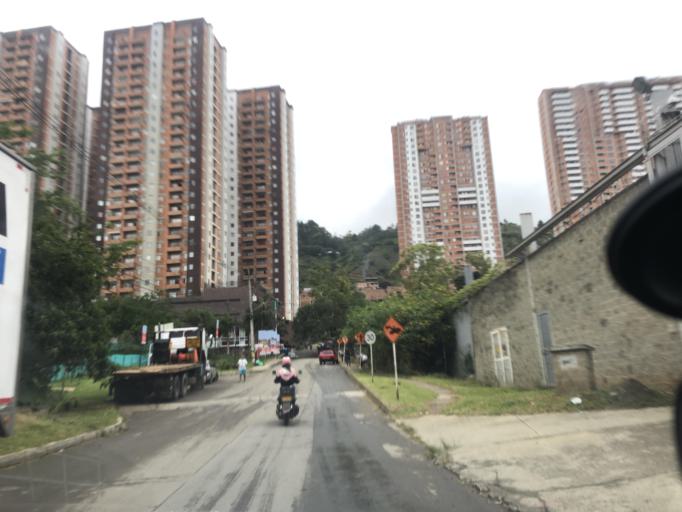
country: CO
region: Antioquia
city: Bello
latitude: 6.3244
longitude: -75.5492
